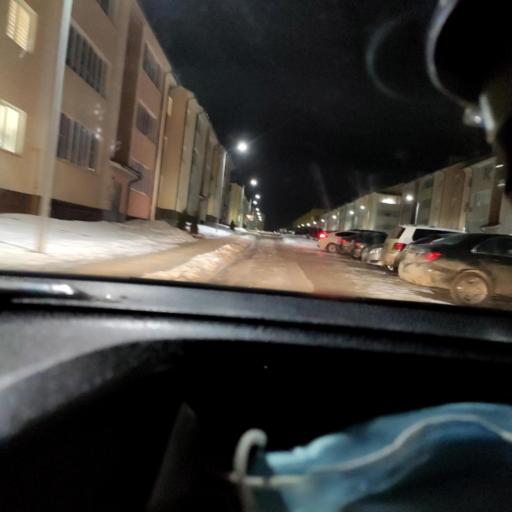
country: RU
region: Voronezj
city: Podgornoye
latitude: 51.7934
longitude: 39.1914
